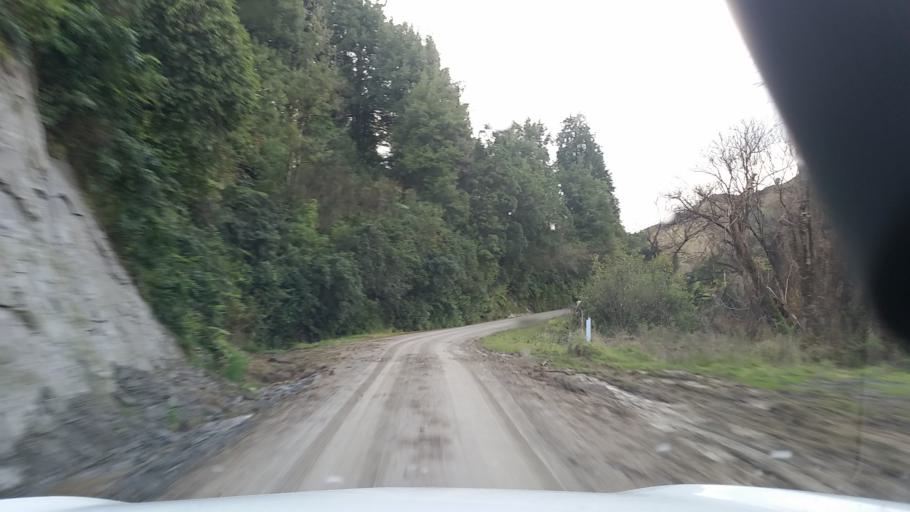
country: NZ
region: Taranaki
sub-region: South Taranaki District
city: Patea
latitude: -39.5627
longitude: 174.8036
